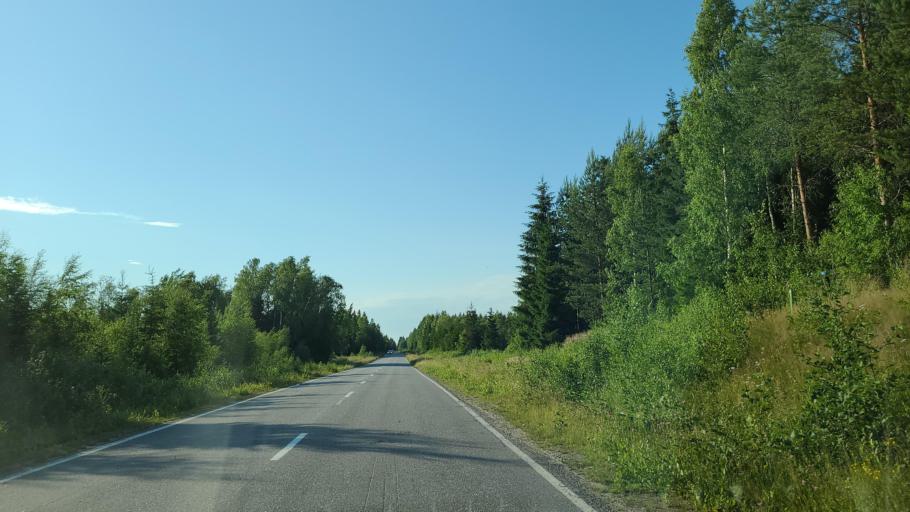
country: FI
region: Ostrobothnia
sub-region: Vaasa
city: Replot
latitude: 63.2569
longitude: 21.3667
